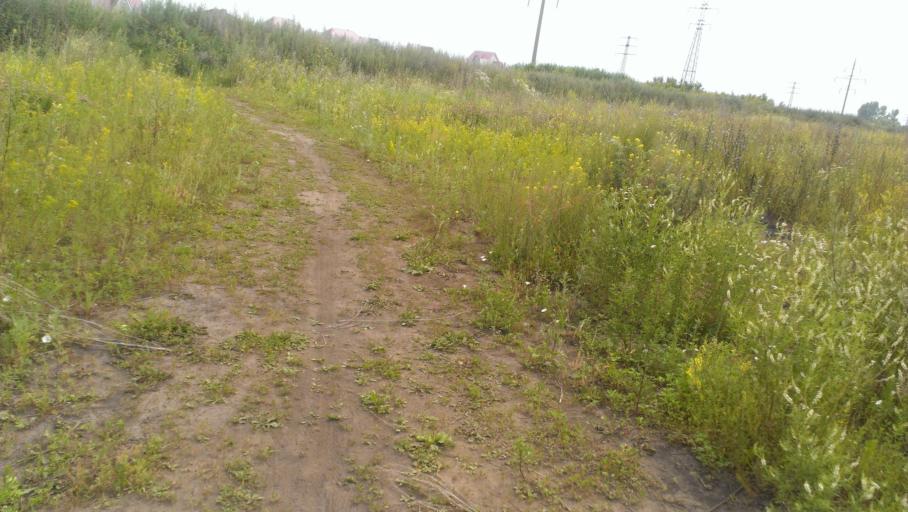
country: RU
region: Altai Krai
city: Novosilikatnyy
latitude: 53.3718
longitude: 83.6482
